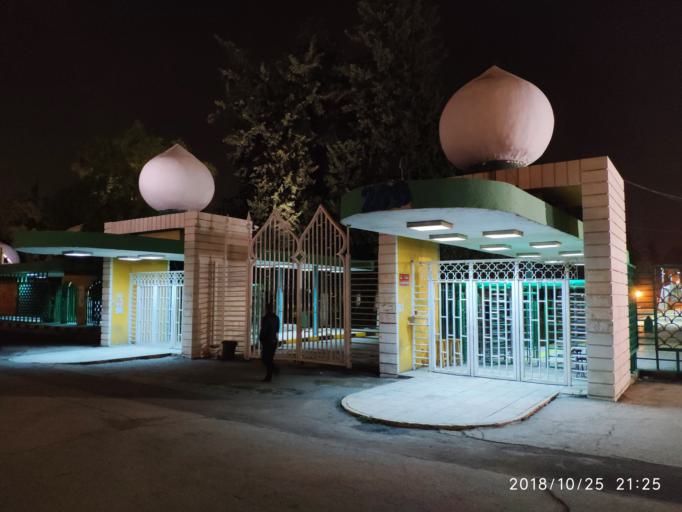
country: JO
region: Amman
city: Al Jubayhah
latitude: 32.0149
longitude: 35.8688
